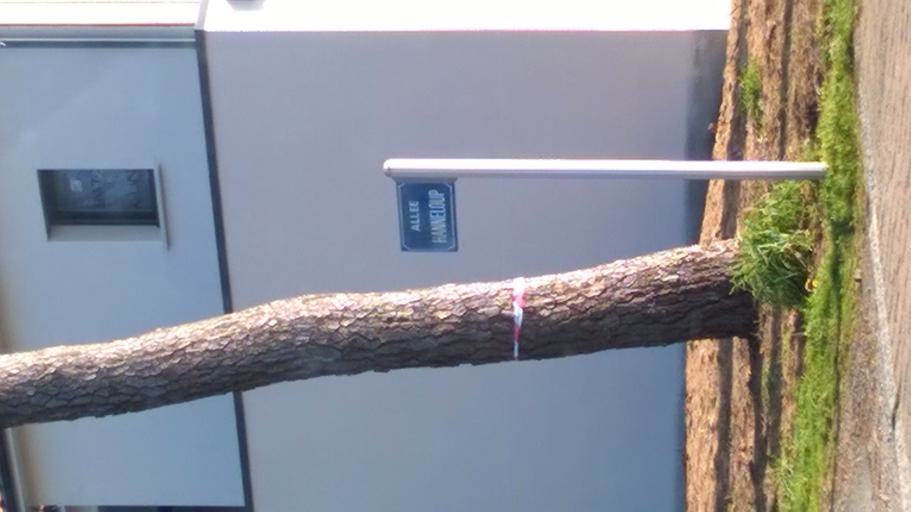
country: FR
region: Pays de la Loire
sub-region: Departement de la Loire-Atlantique
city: Saint-Brevin-les-Pins
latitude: 47.2575
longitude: -2.1698
